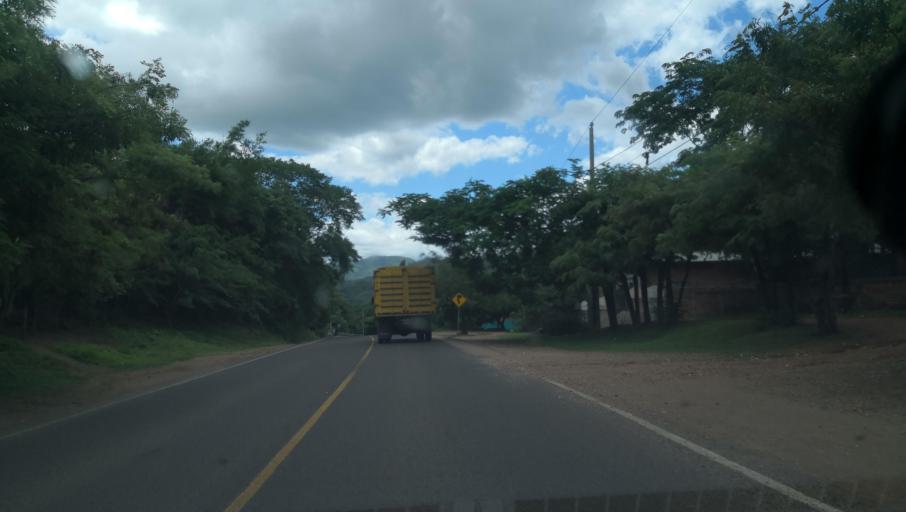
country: NI
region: Madriz
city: Yalaguina
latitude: 13.4635
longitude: -86.4690
